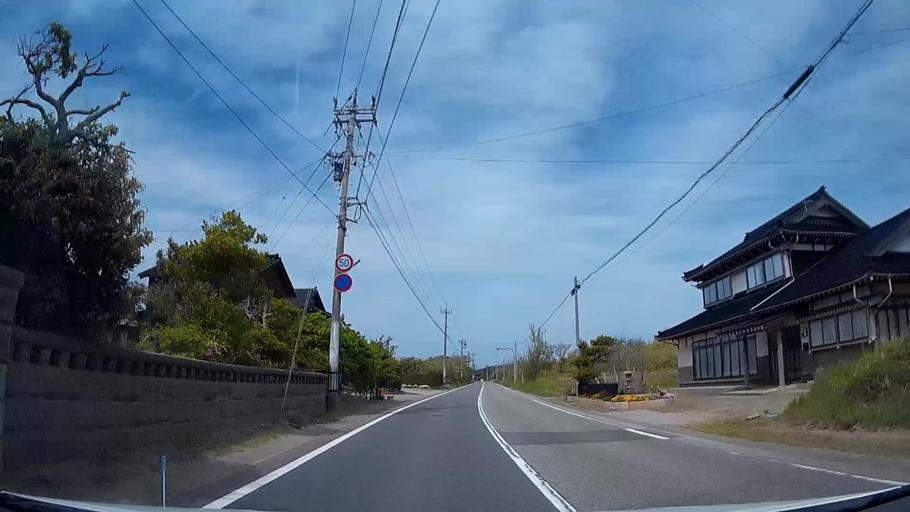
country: JP
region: Ishikawa
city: Hakui
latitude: 36.9702
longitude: 136.7725
